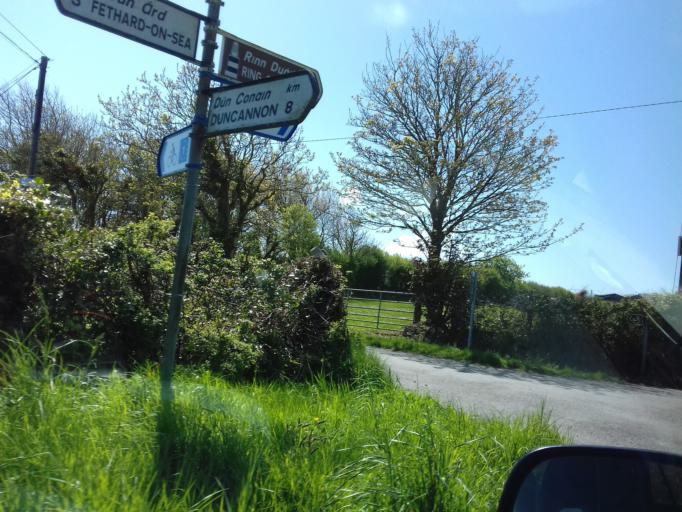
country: IE
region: Munster
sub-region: Waterford
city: Dunmore East
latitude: 52.1775
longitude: -6.8765
